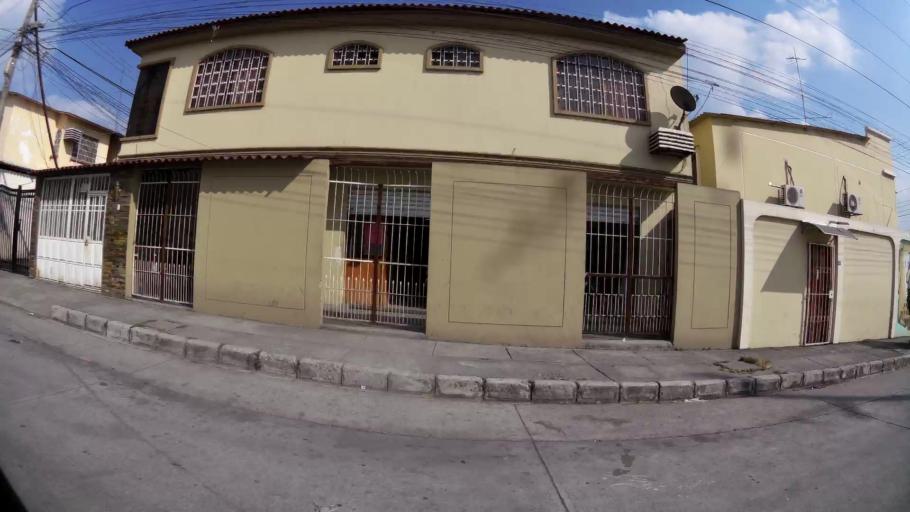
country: EC
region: Guayas
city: Guayaquil
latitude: -2.1315
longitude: -79.9296
